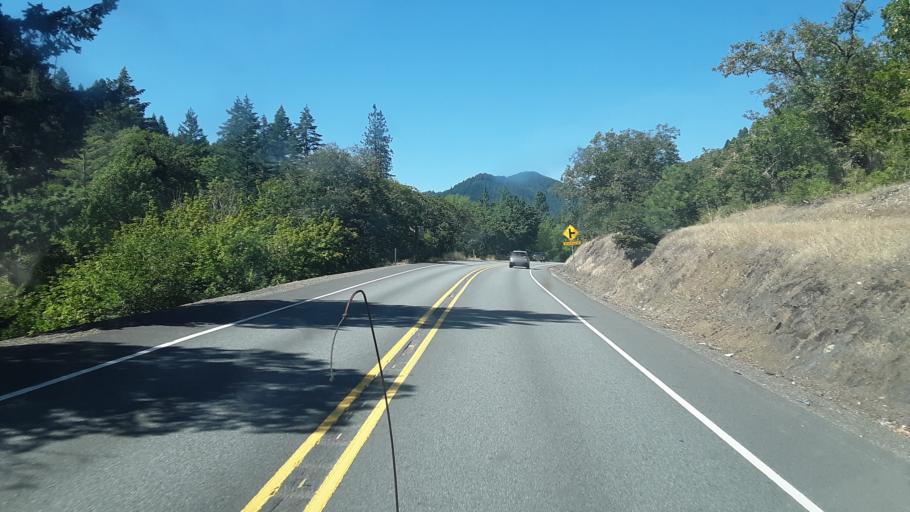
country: US
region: Oregon
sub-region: Josephine County
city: Redwood
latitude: 42.3793
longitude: -123.4927
